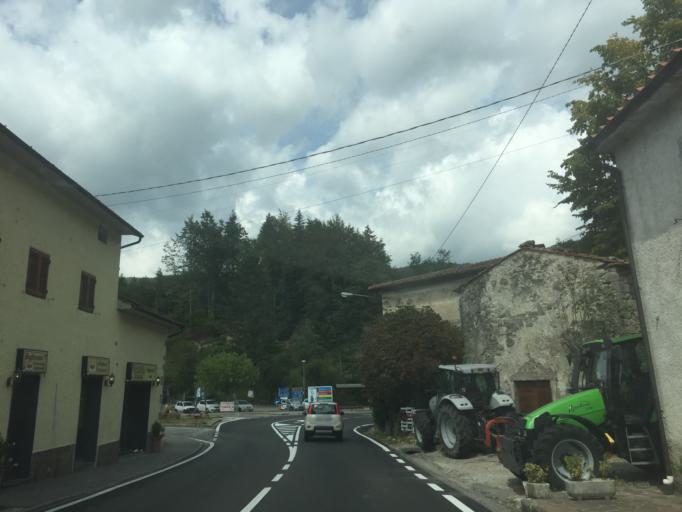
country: IT
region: Tuscany
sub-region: Provincia di Pistoia
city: Campo Tizzoro
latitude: 44.0052
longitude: 10.8361
